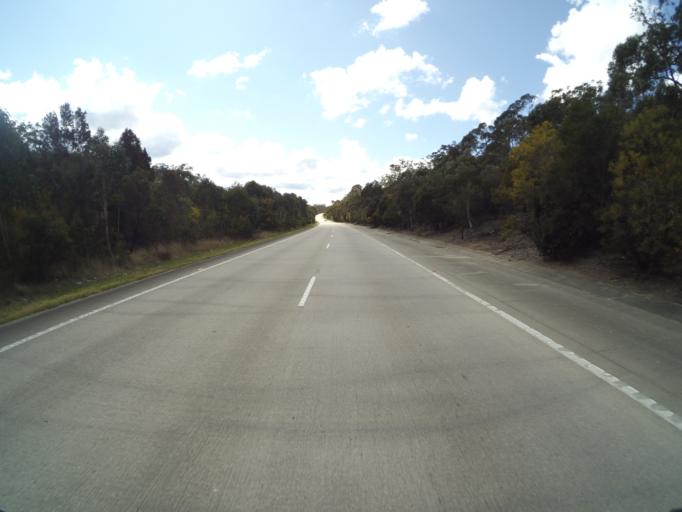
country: AU
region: New South Wales
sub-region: Wingecarribee
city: Mittagong
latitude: -34.4290
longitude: 150.4655
